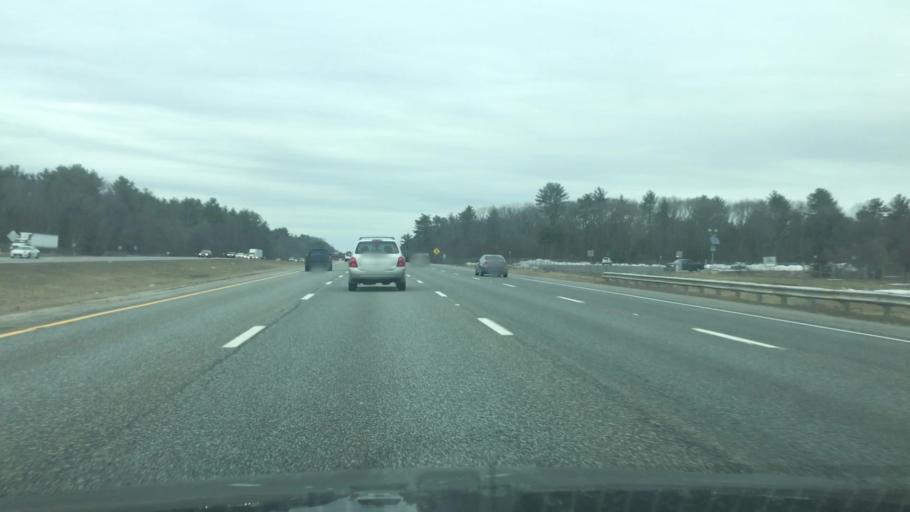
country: US
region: Massachusetts
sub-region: Essex County
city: Boxford
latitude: 42.6952
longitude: -70.9697
